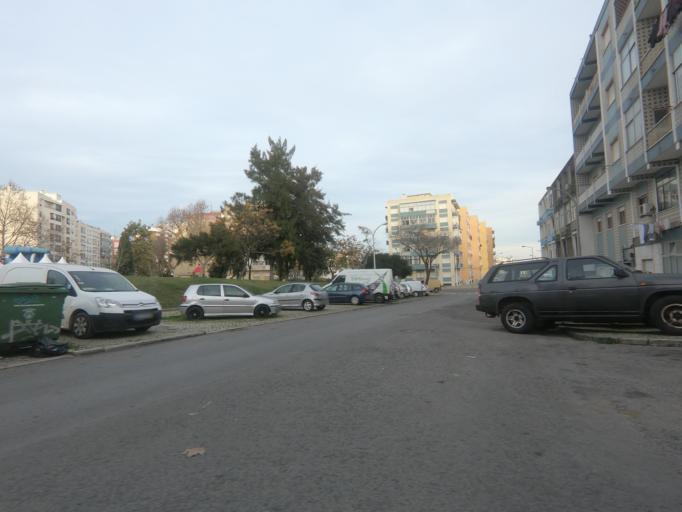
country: PT
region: Setubal
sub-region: Setubal
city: Setubal
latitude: 38.5317
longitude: -8.8697
